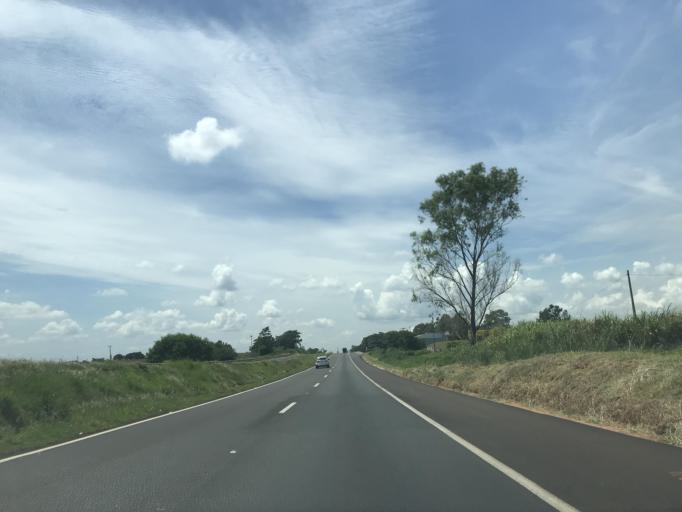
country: BR
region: Parana
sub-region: Alto Parana
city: Alto Parana
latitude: -23.1752
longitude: -52.2340
